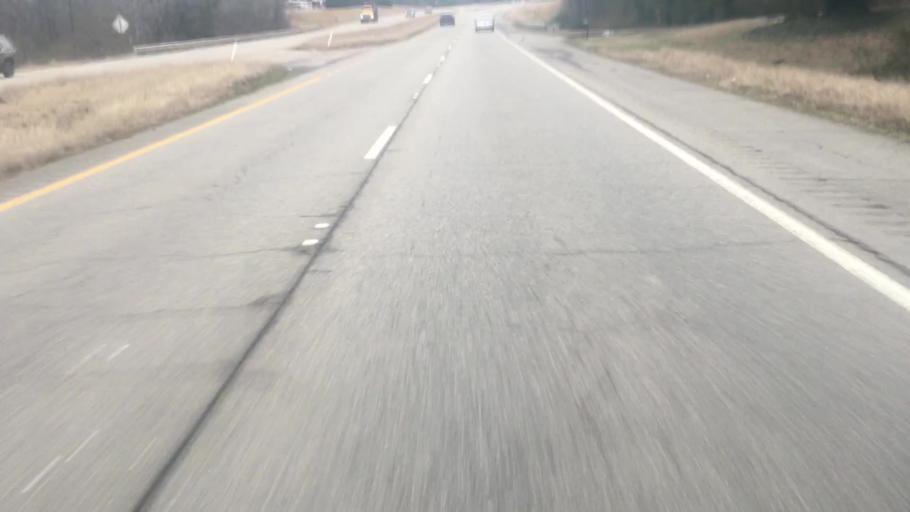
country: US
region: Alabama
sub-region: Walker County
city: Cordova
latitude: 33.8213
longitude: -87.1613
